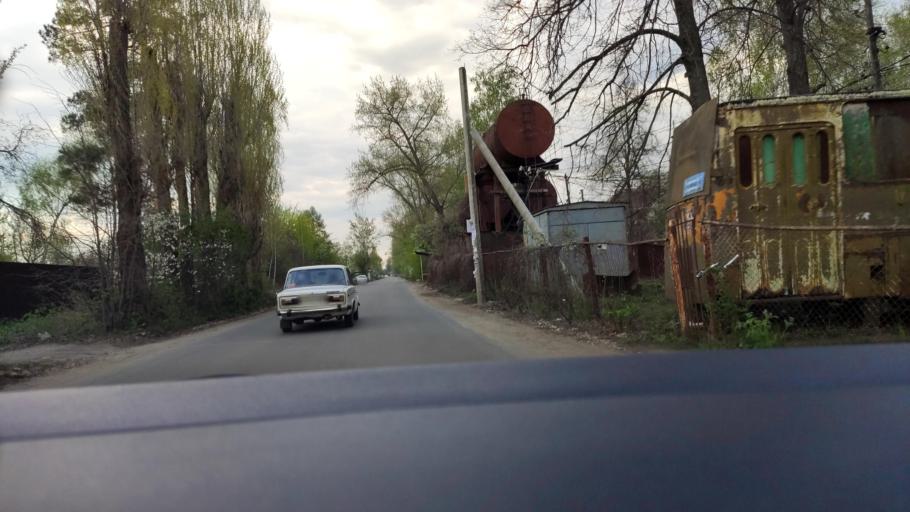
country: RU
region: Voronezj
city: Voronezh
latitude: 51.6017
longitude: 39.1624
